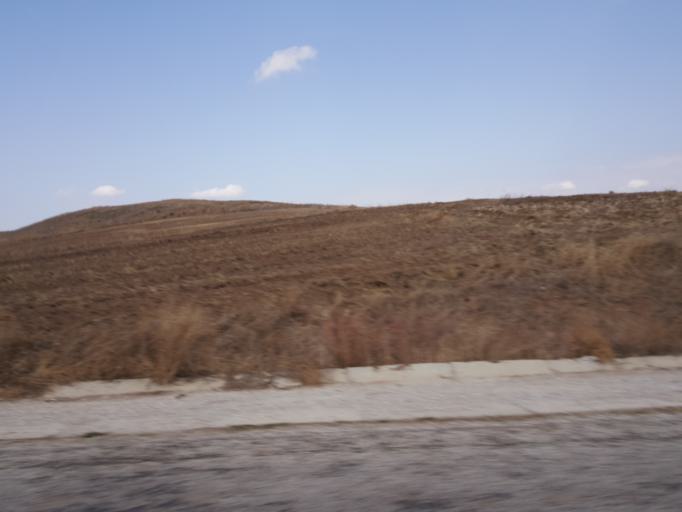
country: TR
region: Corum
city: Alaca
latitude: 40.1559
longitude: 34.7515
